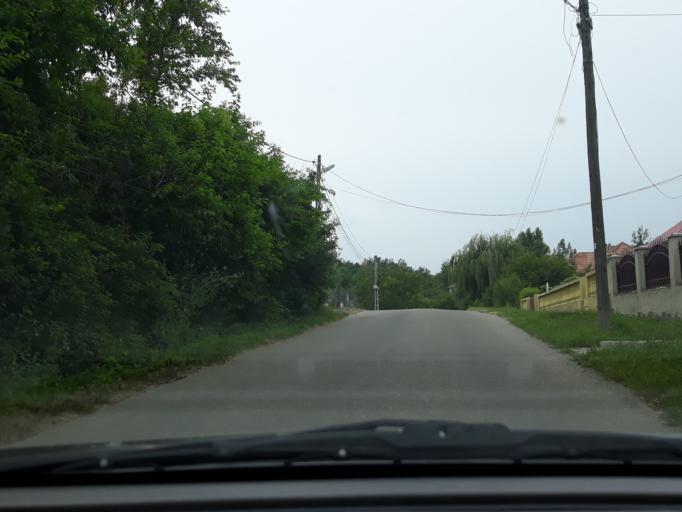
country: RO
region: Salaj
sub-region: Comuna Criseni
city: Criseni
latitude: 47.2502
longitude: 23.0715
